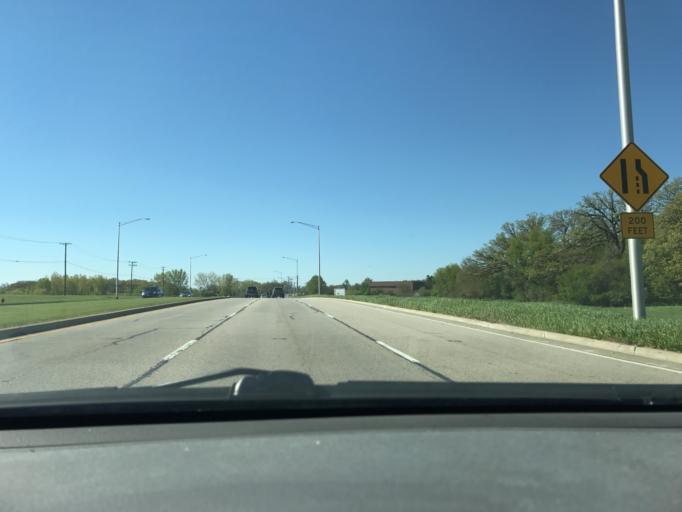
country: US
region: Illinois
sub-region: Kane County
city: Sleepy Hollow
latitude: 42.0691
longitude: -88.3357
